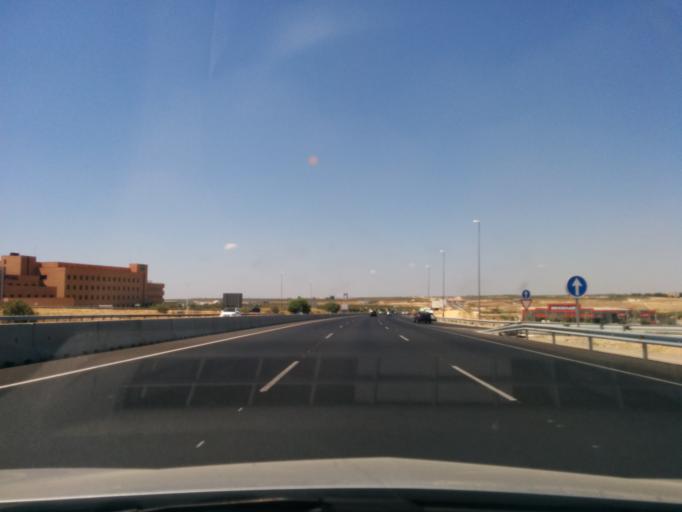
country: ES
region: Andalusia
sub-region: Provincia de Sevilla
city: Bormujos
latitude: 37.3755
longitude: -6.0820
